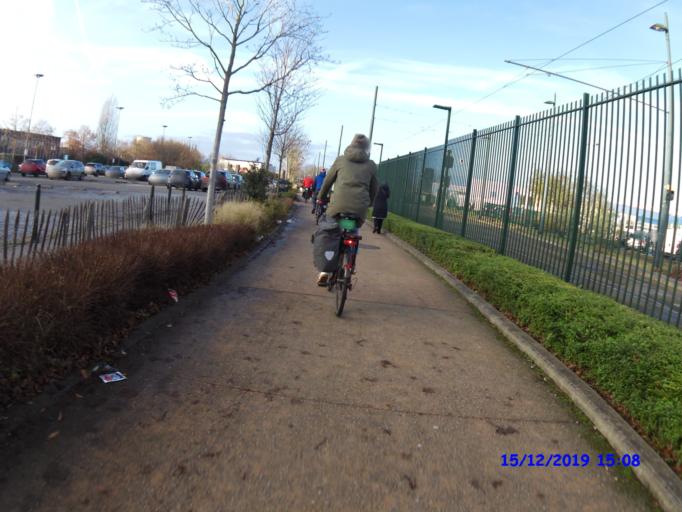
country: BE
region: Flanders
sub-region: Provincie Vlaams-Brabant
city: Drogenbos
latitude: 50.7943
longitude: 4.3197
